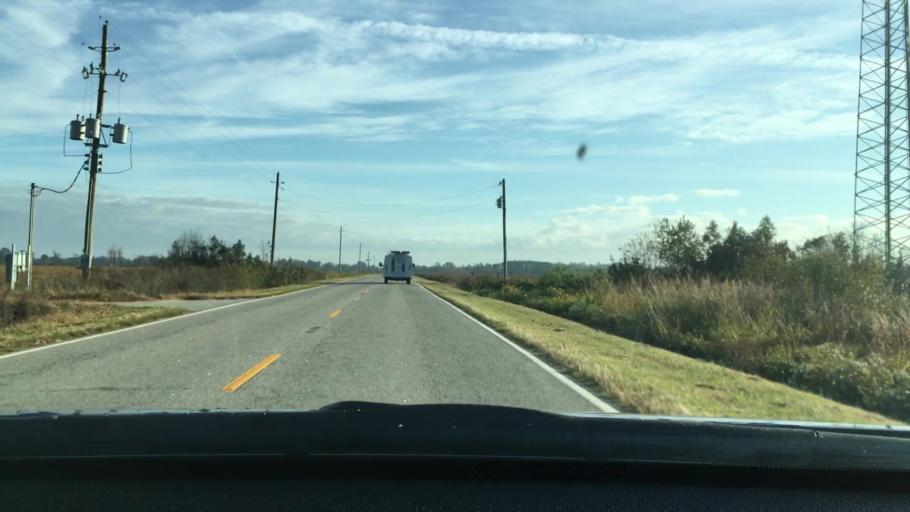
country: US
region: South Carolina
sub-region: Sumter County
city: East Sumter
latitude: 34.0568
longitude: -80.2360
